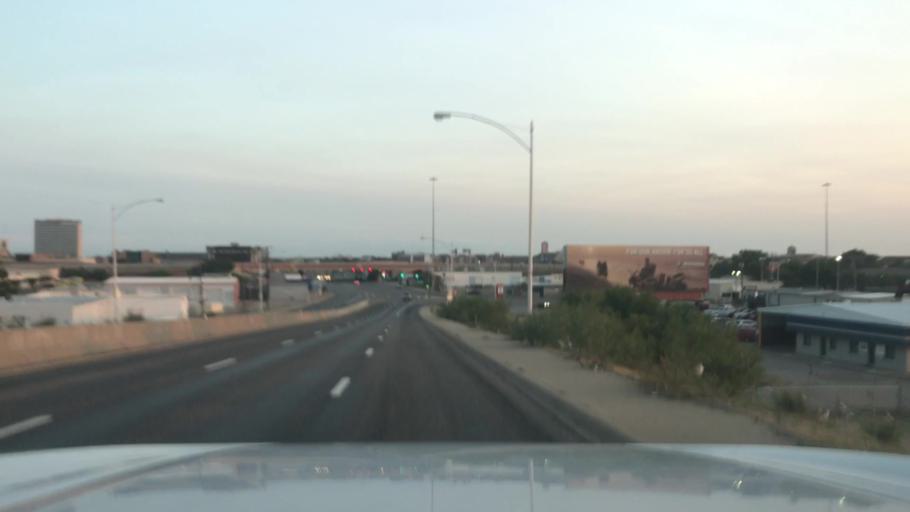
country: US
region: Texas
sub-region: Lubbock County
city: Lubbock
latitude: 33.5965
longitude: -101.8549
